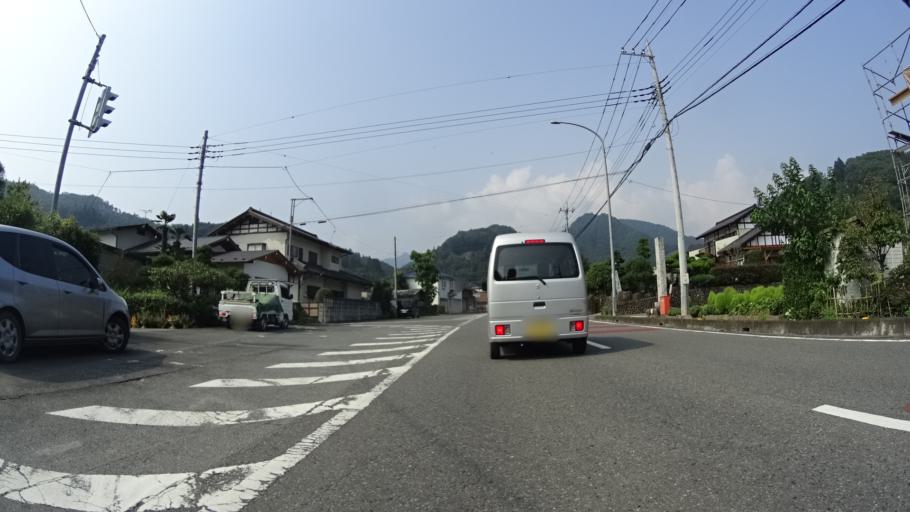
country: JP
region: Saitama
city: Chichibu
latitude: 36.0261
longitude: 138.9697
